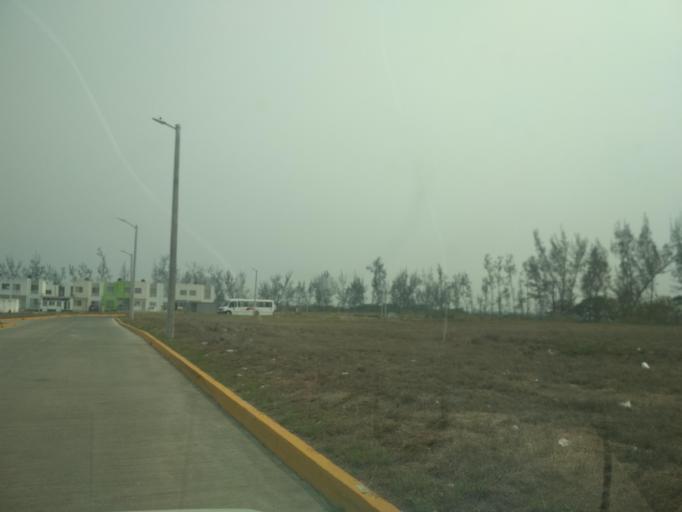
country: MX
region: Veracruz
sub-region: Veracruz
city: Las Amapolas
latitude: 19.1452
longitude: -96.2234
